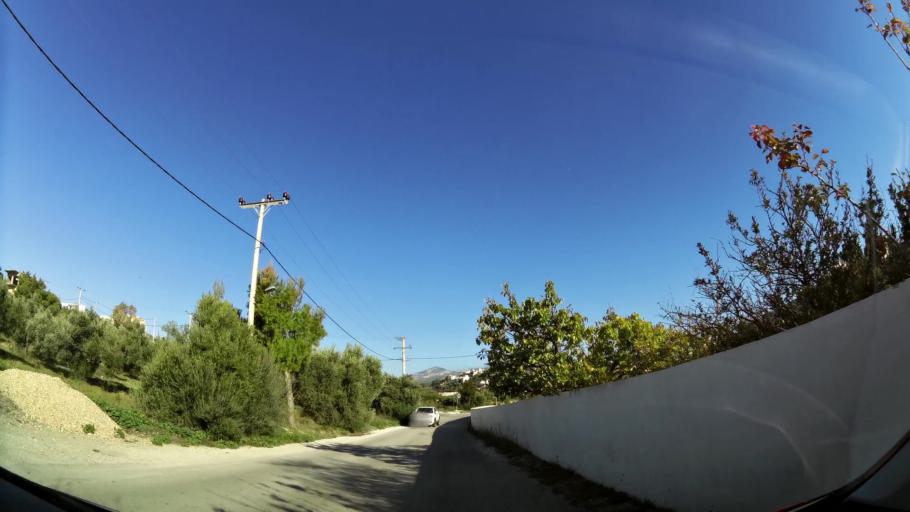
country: GR
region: Attica
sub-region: Nomarchia Anatolikis Attikis
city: Dhrafi
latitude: 38.0152
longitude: 23.9020
